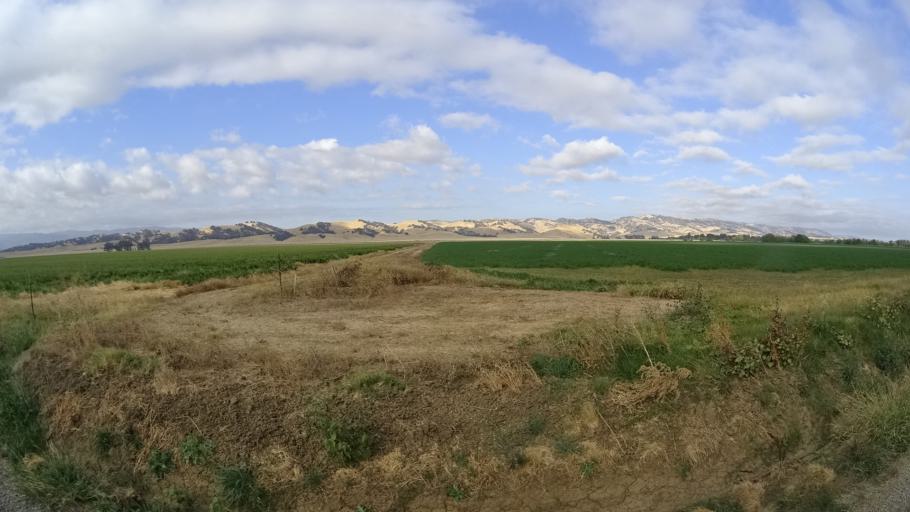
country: US
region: California
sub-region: Yolo County
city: Esparto
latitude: 38.7523
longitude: -122.0444
